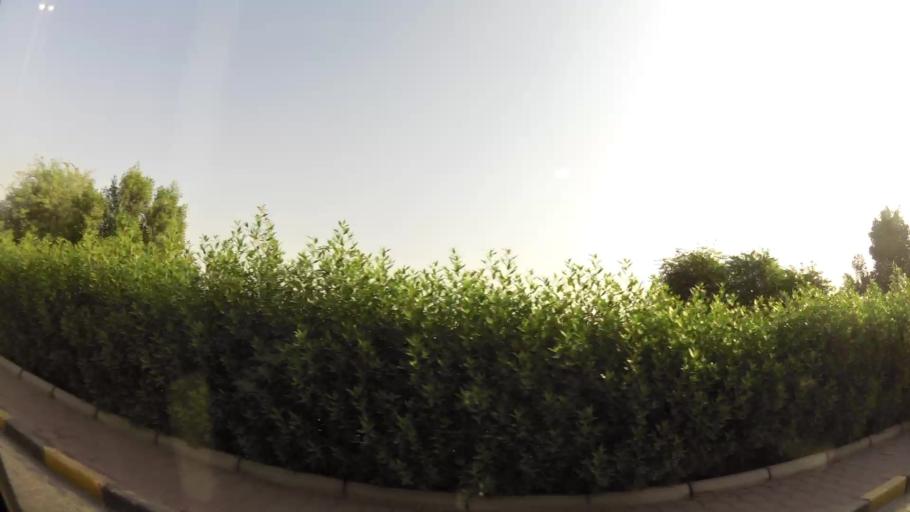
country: KW
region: Al Asimah
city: Ad Dasmah
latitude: 29.3562
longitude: 48.0045
